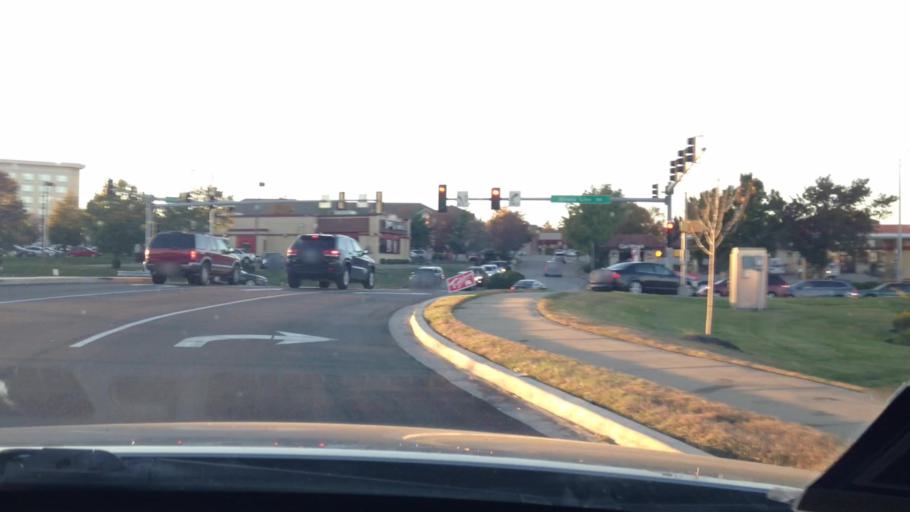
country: US
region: Kansas
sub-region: Johnson County
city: Lenexa
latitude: 38.9106
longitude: -94.7666
